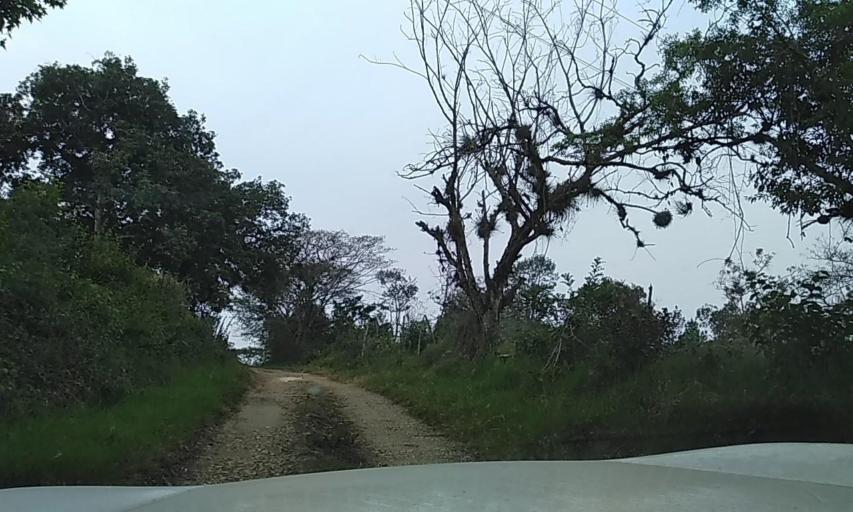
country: MX
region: Veracruz
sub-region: Xalapa
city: Lomas Verdes
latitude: 19.5011
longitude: -96.9164
